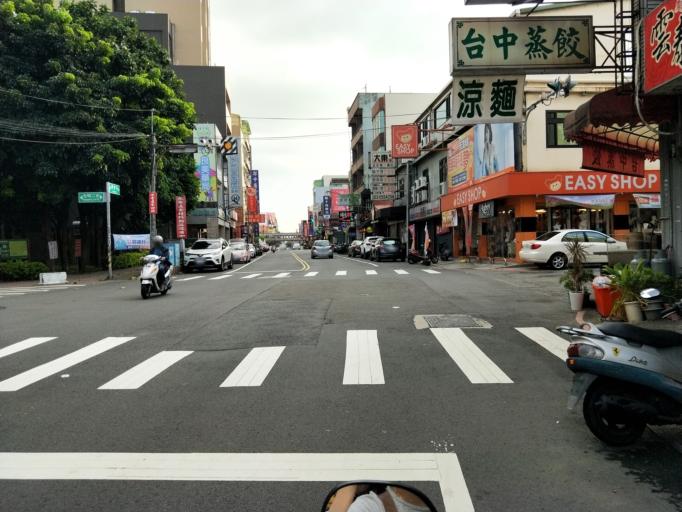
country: TW
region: Taiwan
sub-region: Hsinchu
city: Zhubei
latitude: 24.8329
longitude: 121.0060
